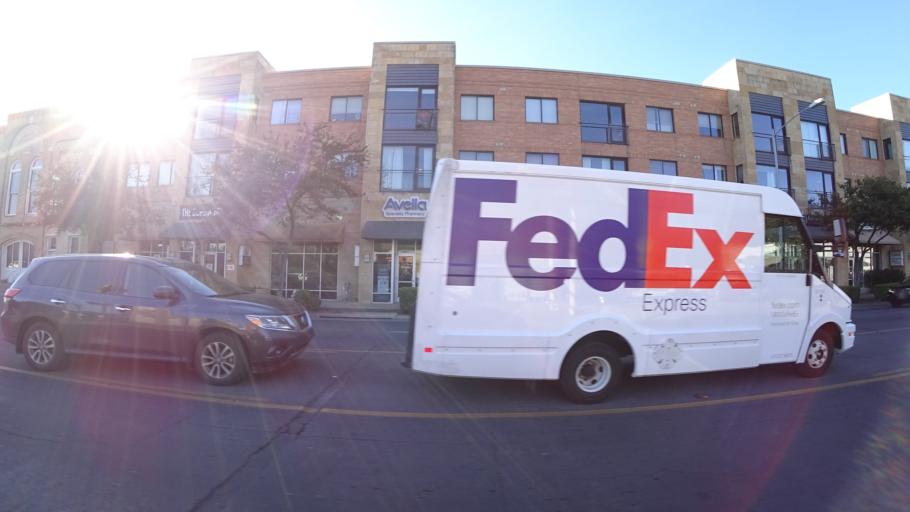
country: US
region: Texas
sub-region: Travis County
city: Austin
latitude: 30.2972
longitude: -97.7416
